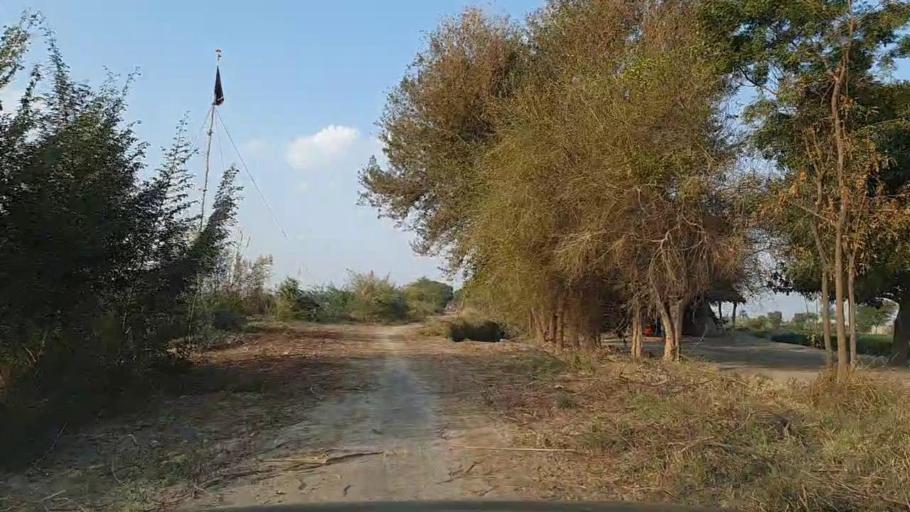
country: PK
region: Sindh
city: Jam Sahib
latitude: 26.3407
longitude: 68.5815
